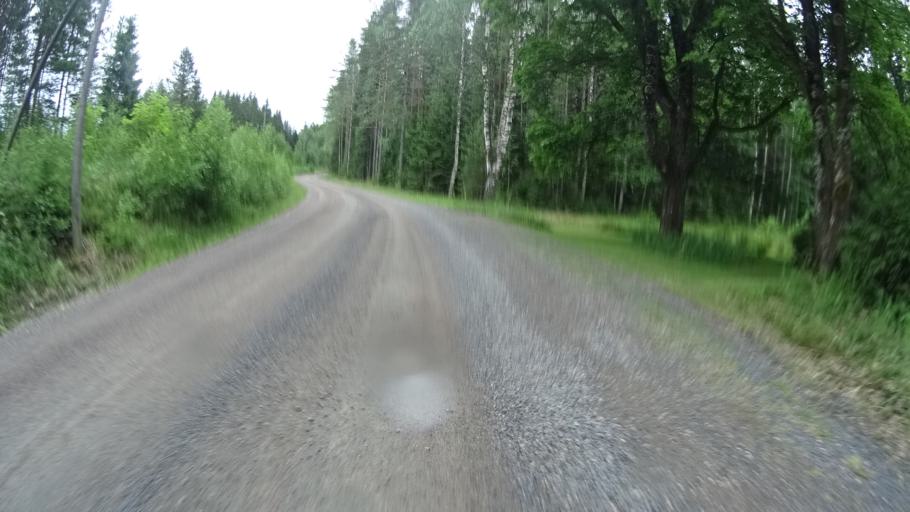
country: FI
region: Uusimaa
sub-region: Helsinki
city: Karkkila
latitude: 60.6000
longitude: 24.1855
